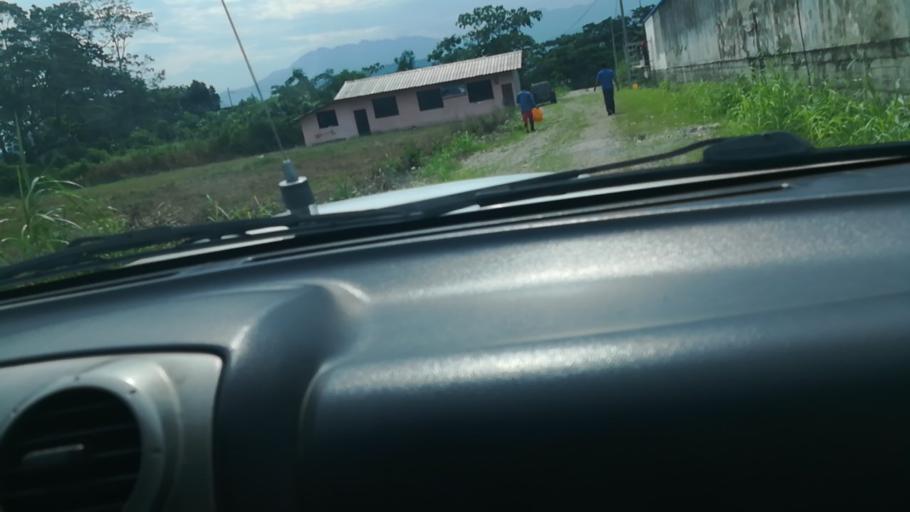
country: EC
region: Napo
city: Tena
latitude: -0.9885
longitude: -77.8204
